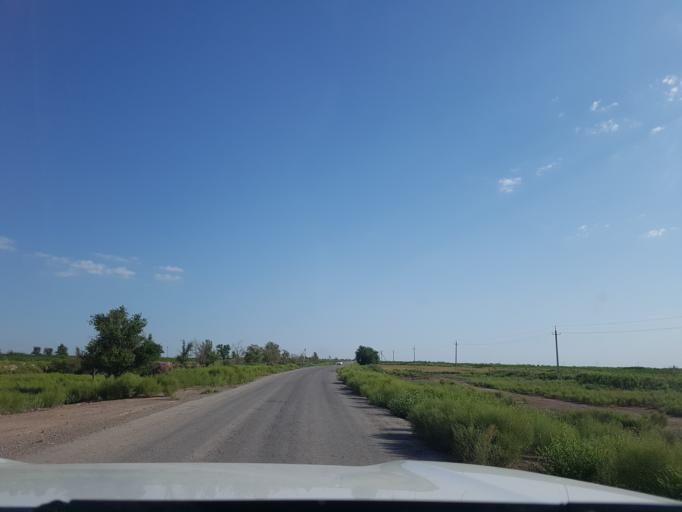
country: TM
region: Dasoguz
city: Koeneuergench
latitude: 41.8971
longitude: 58.7072
